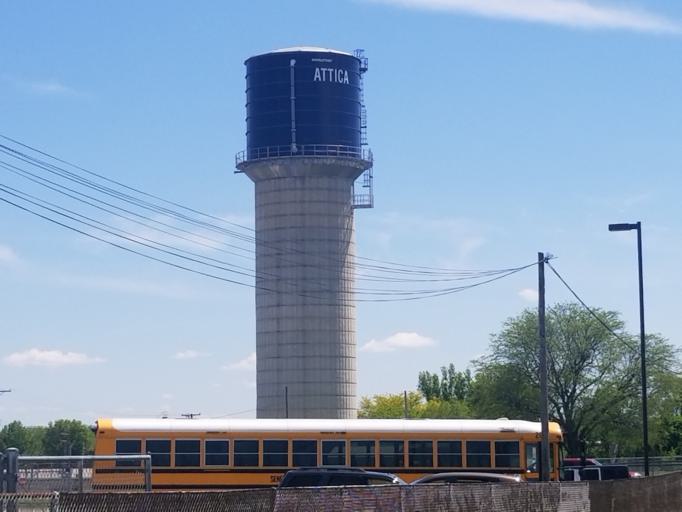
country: US
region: Ohio
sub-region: Huron County
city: Willard
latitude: 41.0661
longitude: -82.8822
